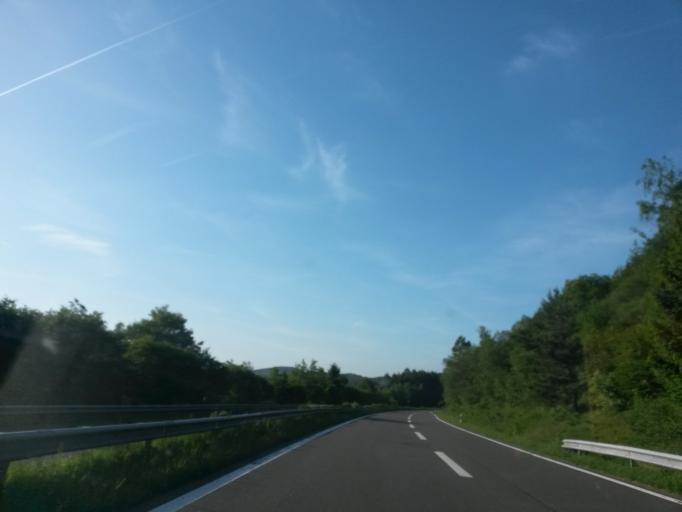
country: DE
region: North Rhine-Westphalia
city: Bergneustadt
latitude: 50.9981
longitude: 7.6374
